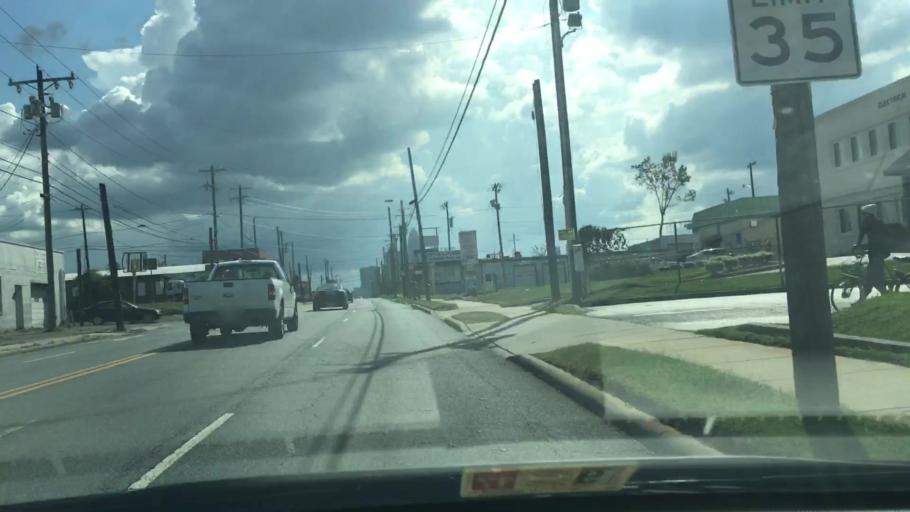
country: US
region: North Carolina
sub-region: Mecklenburg County
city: Charlotte
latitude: 35.2469
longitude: -80.8183
